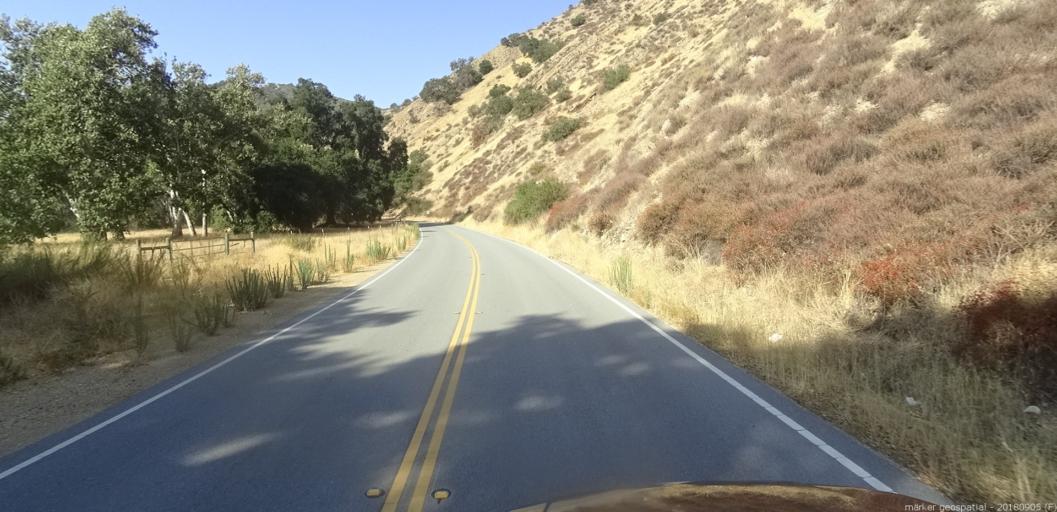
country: US
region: California
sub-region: Monterey County
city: Greenfield
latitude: 36.2575
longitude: -121.4289
